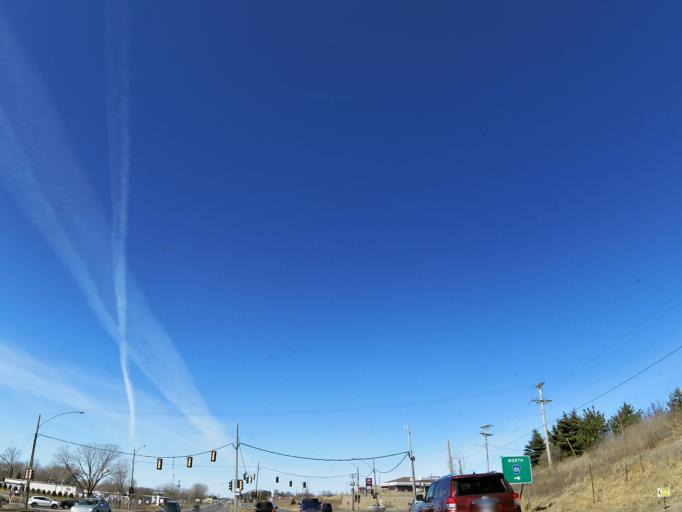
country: US
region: Minnesota
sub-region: Hennepin County
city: Corcoran
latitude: 45.0433
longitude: -93.5241
